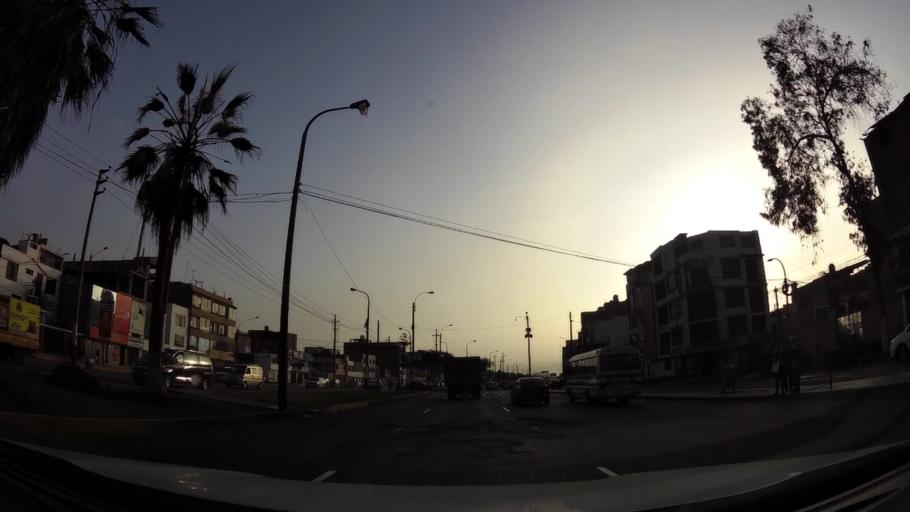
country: PE
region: Lima
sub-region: Lima
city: Independencia
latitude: -11.9916
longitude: -77.0746
